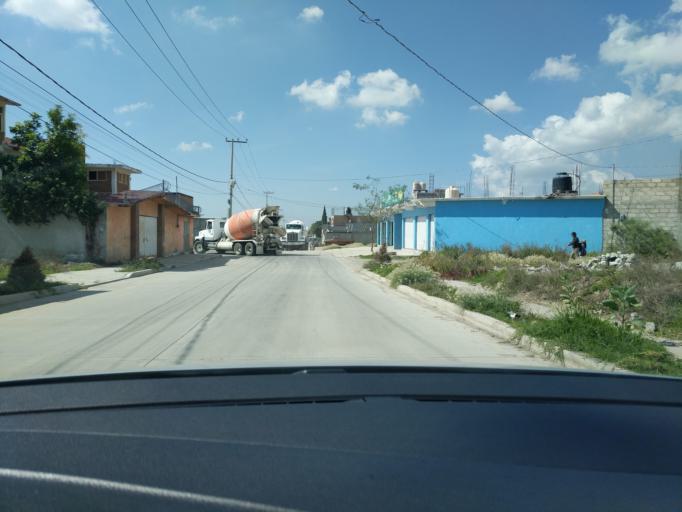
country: MX
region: Hidalgo
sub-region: Zempoala
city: El Mirador
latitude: 20.0252
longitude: -98.8130
